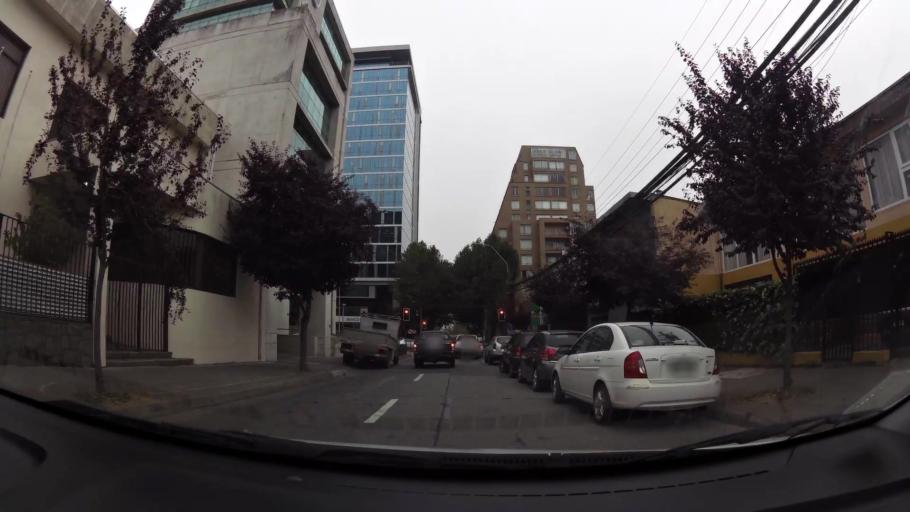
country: CL
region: Biobio
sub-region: Provincia de Concepcion
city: Concepcion
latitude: -36.8329
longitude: -73.0562
